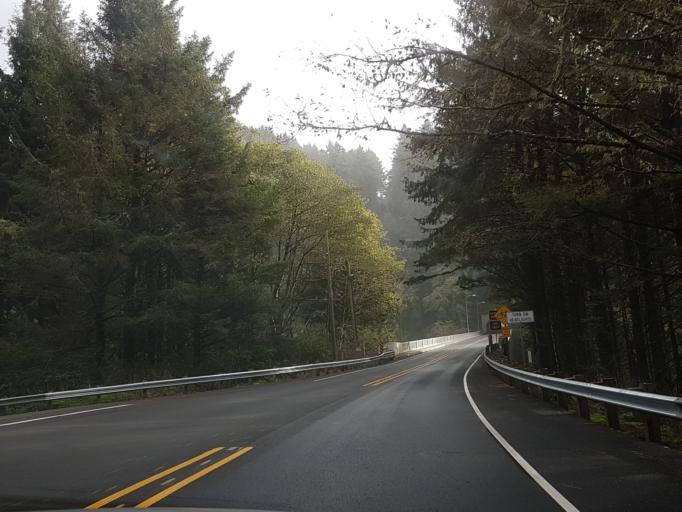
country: US
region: Oregon
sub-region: Lane County
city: Florence
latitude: 44.1350
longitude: -124.1216
